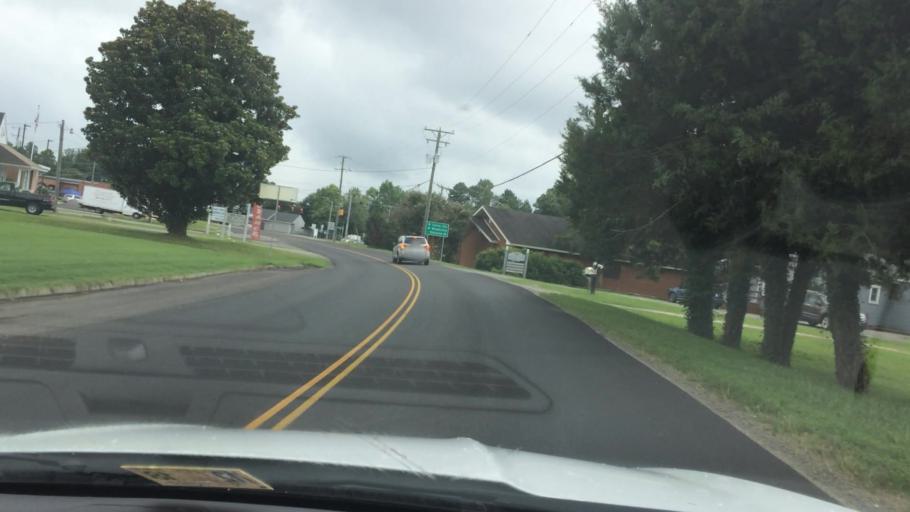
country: US
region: Virginia
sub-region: New Kent County
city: New Kent
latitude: 37.4440
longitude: -77.0445
